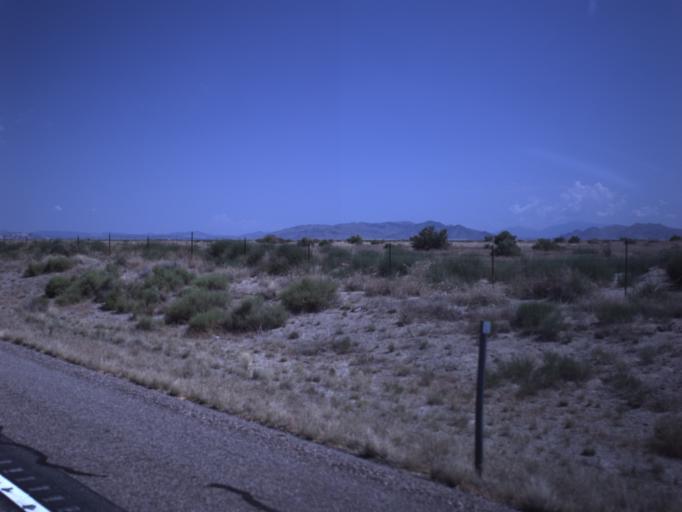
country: US
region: Utah
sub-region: Millard County
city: Delta
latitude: 39.3739
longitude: -112.4964
